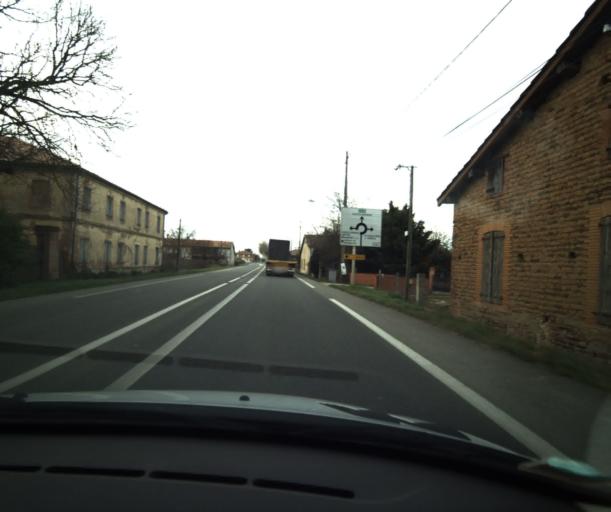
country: FR
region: Midi-Pyrenees
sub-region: Departement du Tarn-et-Garonne
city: Saint-Porquier
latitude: 44.0120
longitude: 1.1711
